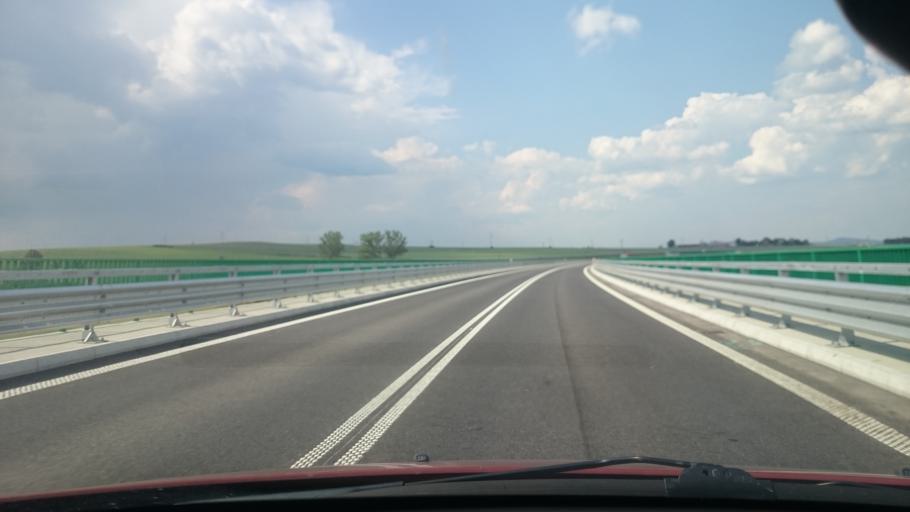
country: PL
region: Lower Silesian Voivodeship
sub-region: Powiat klodzki
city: Klodzko
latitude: 50.4143
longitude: 16.6264
